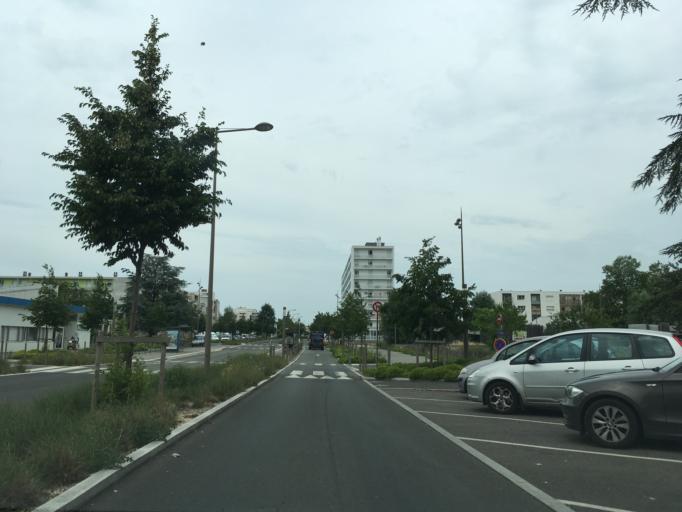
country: FR
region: Poitou-Charentes
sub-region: Departement des Deux-Sevres
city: Niort
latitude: 46.3145
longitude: -0.4813
